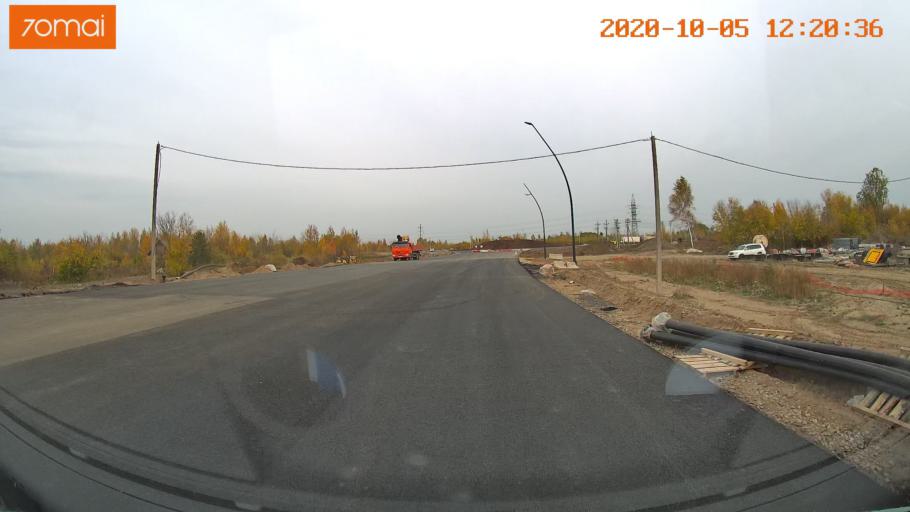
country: RU
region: Ivanovo
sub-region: Gorod Ivanovo
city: Ivanovo
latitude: 56.9648
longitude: 40.9310
